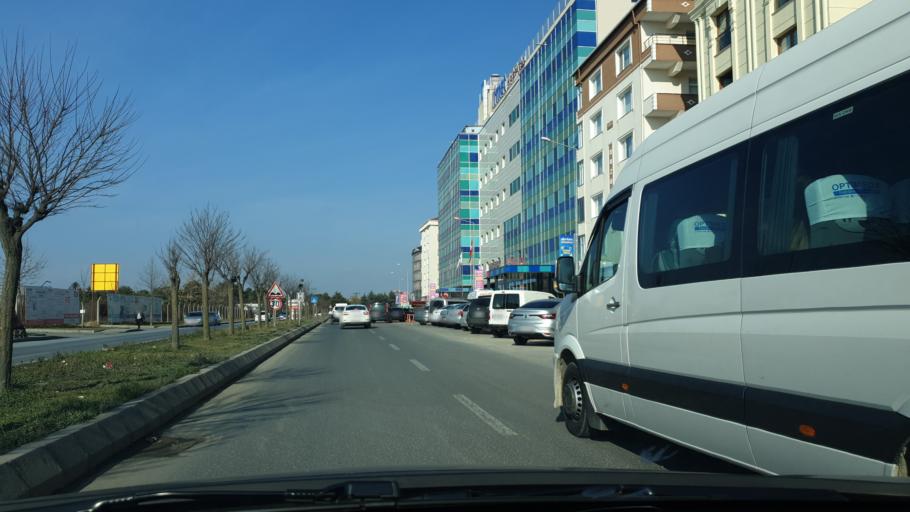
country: TR
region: Tekirdag
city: Cerkezkoey
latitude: 41.2929
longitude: 27.9943
